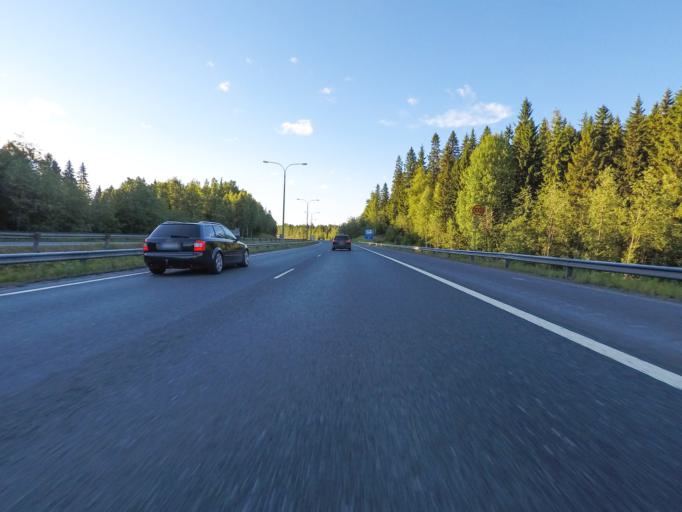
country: FI
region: Northern Savo
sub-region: Kuopio
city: Kuopio
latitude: 62.8506
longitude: 27.6206
